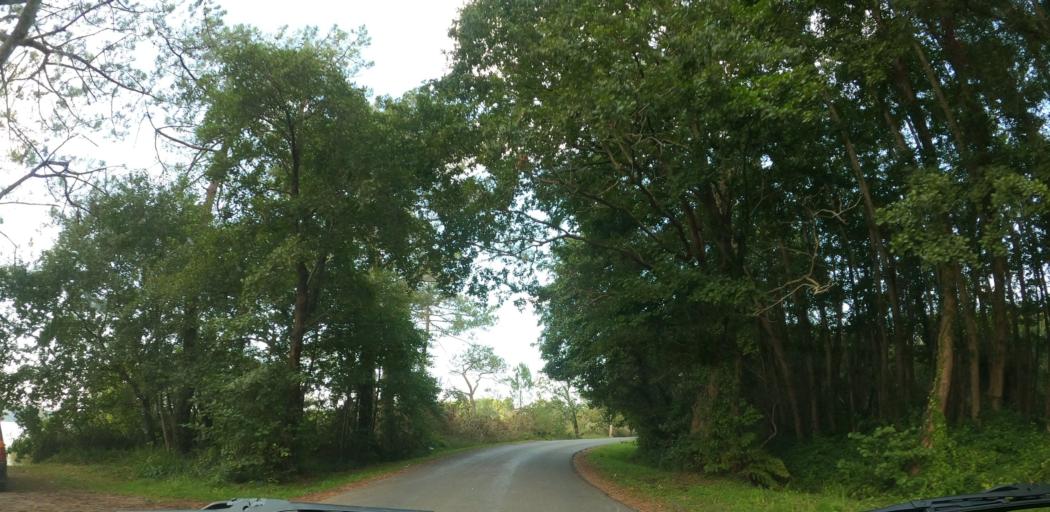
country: FR
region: Aquitaine
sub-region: Departement des Landes
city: Seignosse
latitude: 43.7160
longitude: -1.3583
